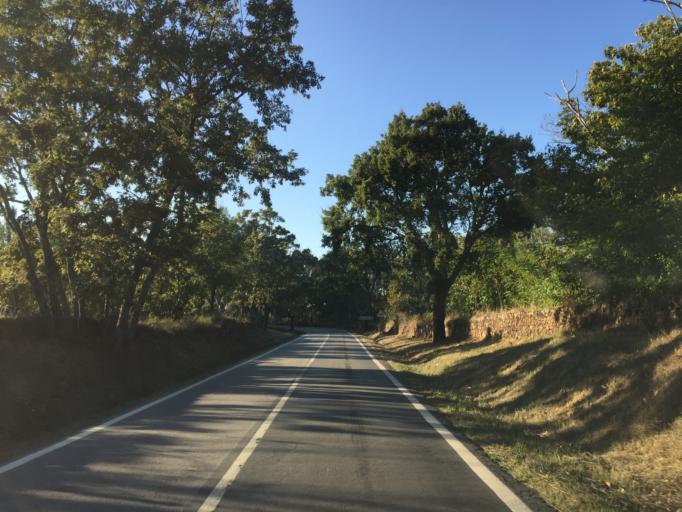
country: PT
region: Portalegre
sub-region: Castelo de Vide
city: Castelo de Vide
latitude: 39.3971
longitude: -7.4254
